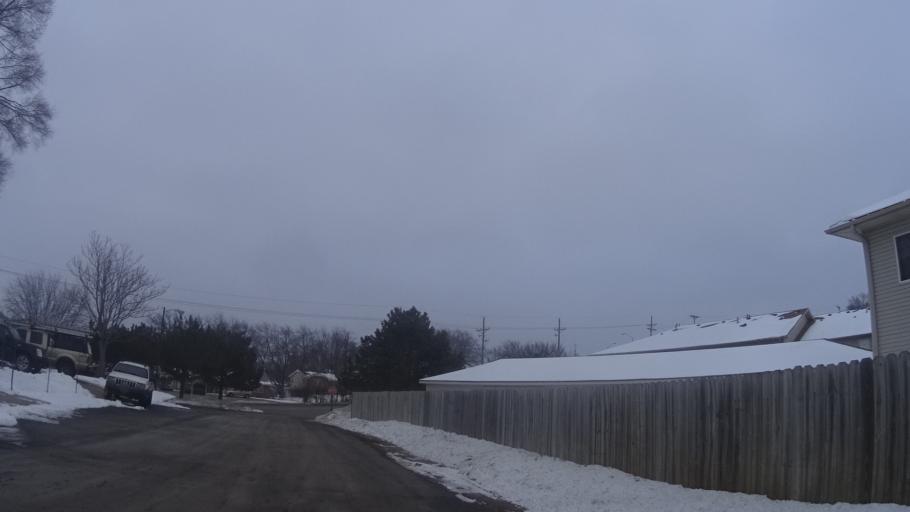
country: US
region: Nebraska
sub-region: Sarpy County
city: Offutt Air Force Base
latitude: 41.1395
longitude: -95.9205
